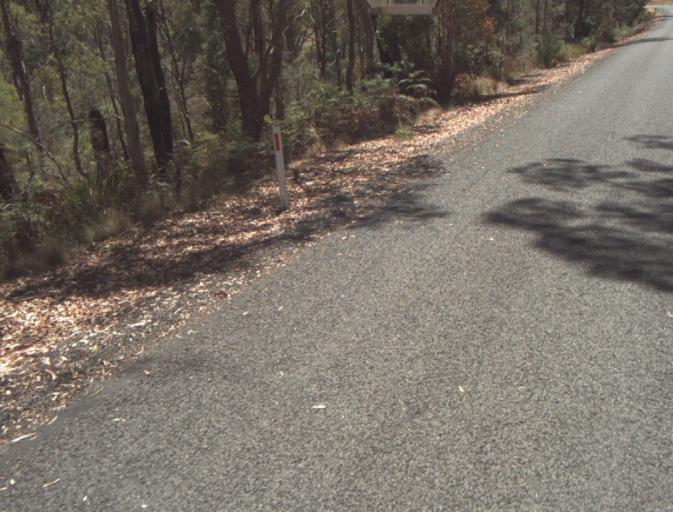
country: AU
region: Tasmania
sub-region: Launceston
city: Newstead
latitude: -41.3684
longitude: 147.3006
